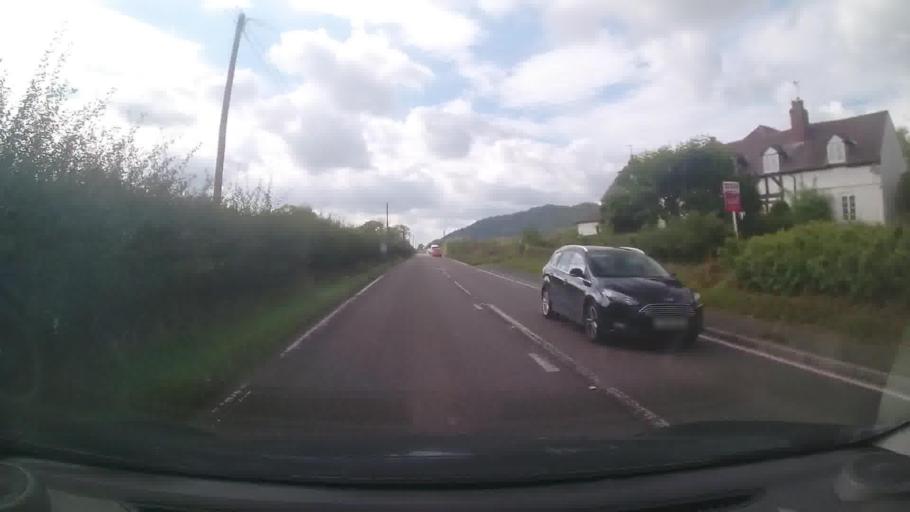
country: GB
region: Wales
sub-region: Sir Powys
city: Welshpool
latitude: 52.6940
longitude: -3.1028
